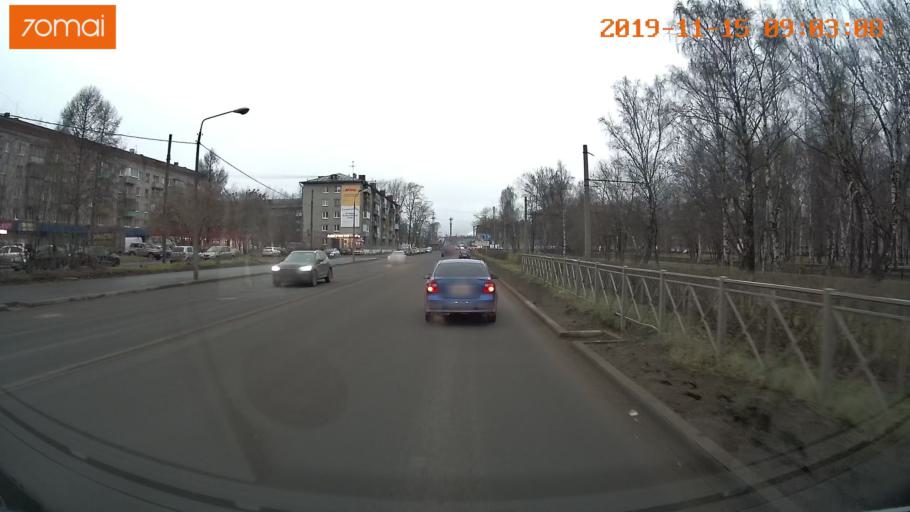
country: RU
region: Vologda
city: Cherepovets
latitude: 59.1375
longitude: 37.9243
